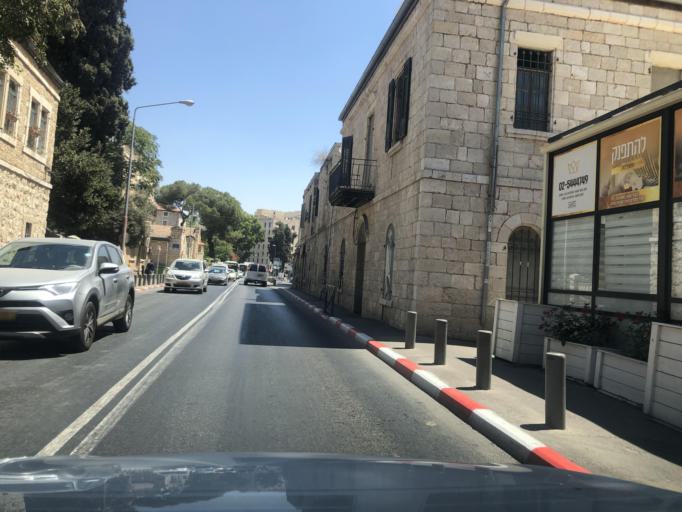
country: IL
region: Jerusalem
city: West Jerusalem
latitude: 31.7842
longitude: 35.2197
